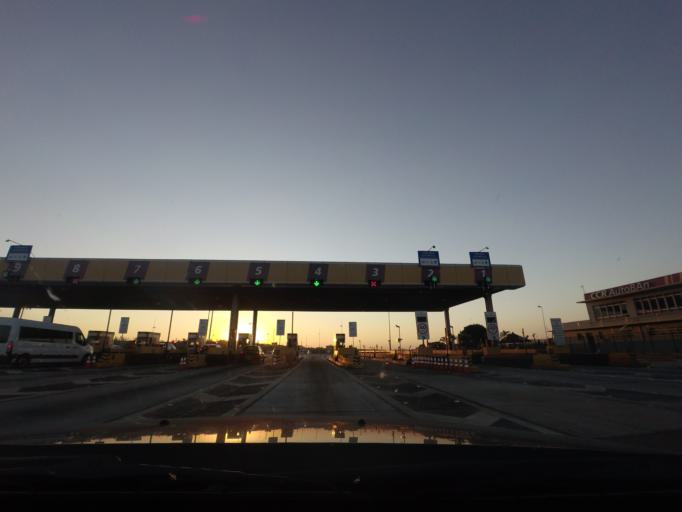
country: BR
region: Sao Paulo
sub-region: Sumare
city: Sumare
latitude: -22.8573
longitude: -47.3002
